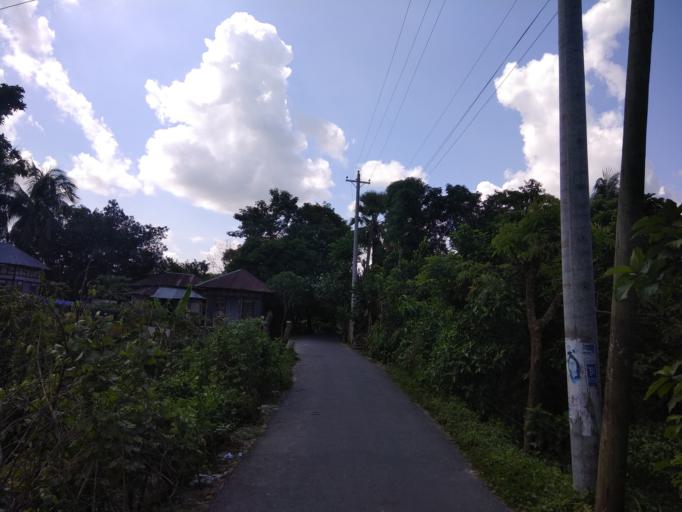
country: BD
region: Dhaka
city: Narayanganj
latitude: 23.4431
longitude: 90.4740
